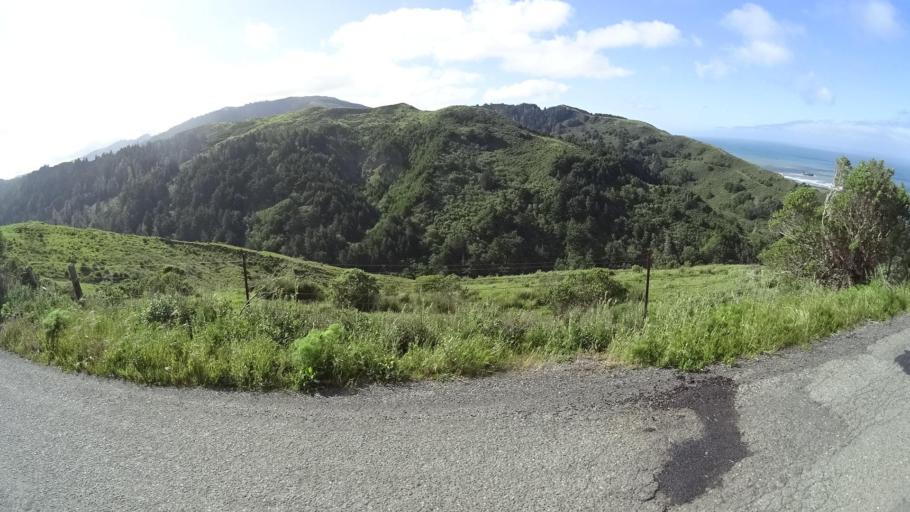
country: US
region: California
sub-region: Humboldt County
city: Ferndale
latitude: 40.4352
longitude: -124.3937
